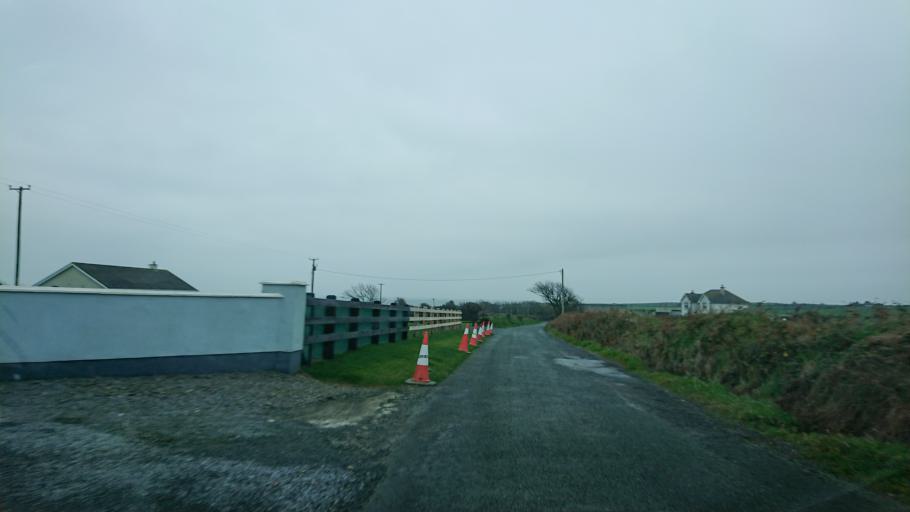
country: IE
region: Munster
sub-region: Waterford
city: Dunmore East
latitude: 52.1526
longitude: -7.0584
